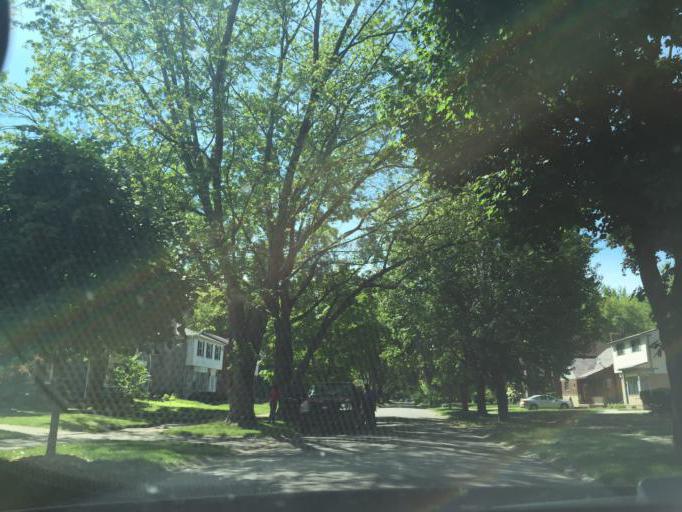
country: US
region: Michigan
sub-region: Oakland County
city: Oak Park
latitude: 42.4030
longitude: -83.2214
